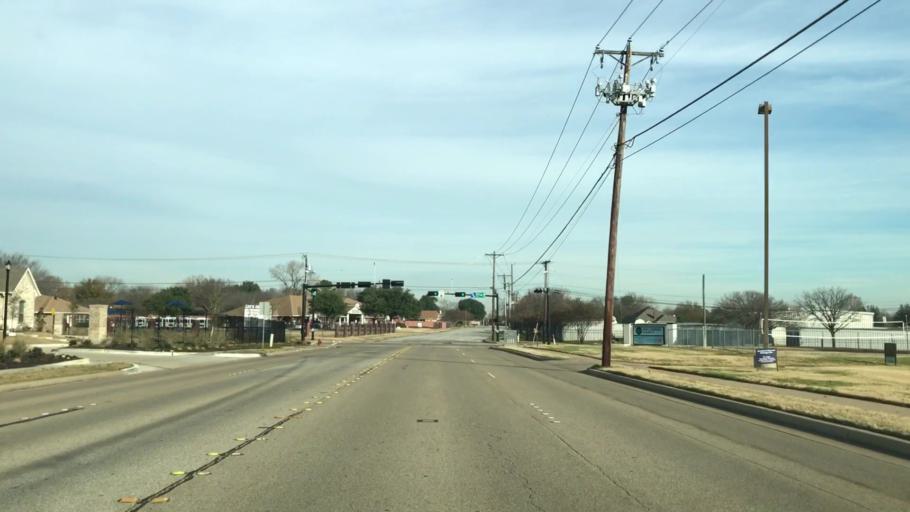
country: US
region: Texas
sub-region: Tarrant County
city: Watauga
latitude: 32.8814
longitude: -97.2119
